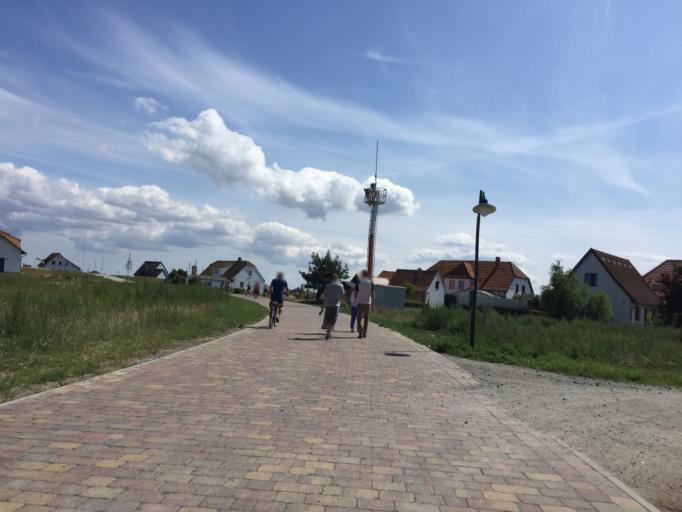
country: DE
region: Mecklenburg-Vorpommern
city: Hiddensee
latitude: 54.5253
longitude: 13.0886
